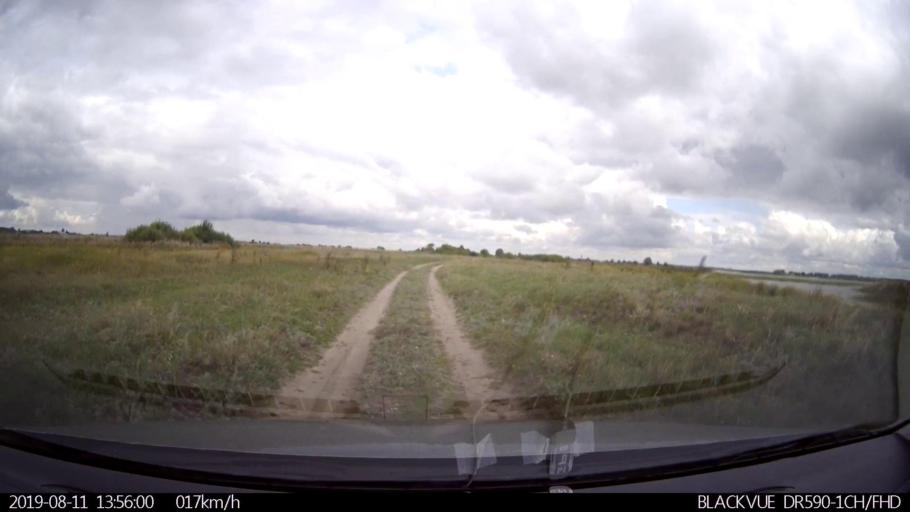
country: RU
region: Ulyanovsk
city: Ignatovka
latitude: 53.8465
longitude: 47.5876
